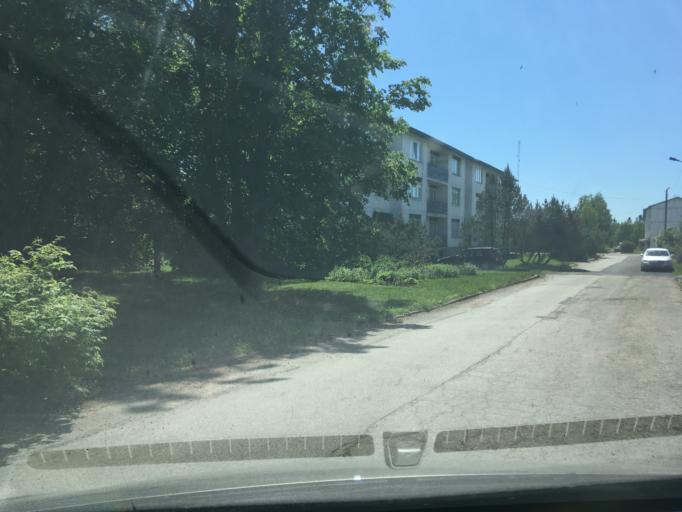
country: EE
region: Laeaene
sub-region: Lihula vald
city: Lihula
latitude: 58.6892
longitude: 23.8417
